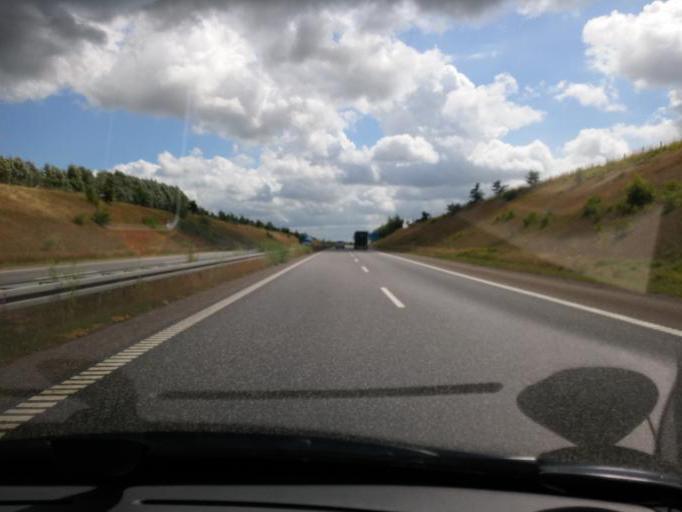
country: DK
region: South Denmark
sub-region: Faaborg-Midtfyn Kommune
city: Arslev
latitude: 55.2763
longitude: 10.4596
